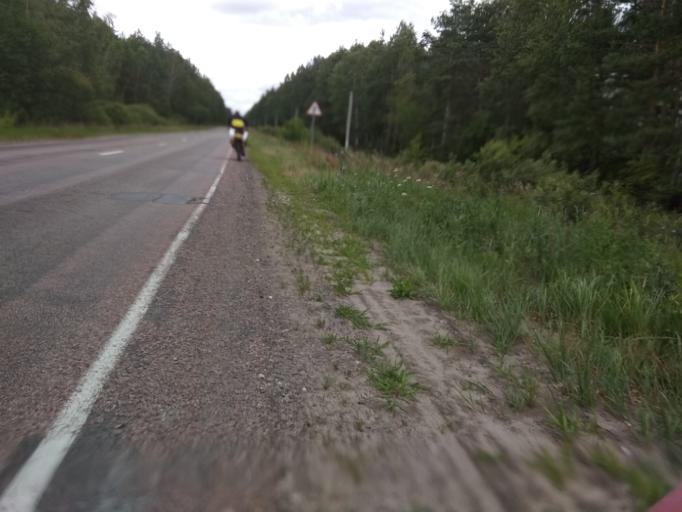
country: RU
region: Moskovskaya
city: Misheronskiy
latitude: 55.6096
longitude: 39.7150
